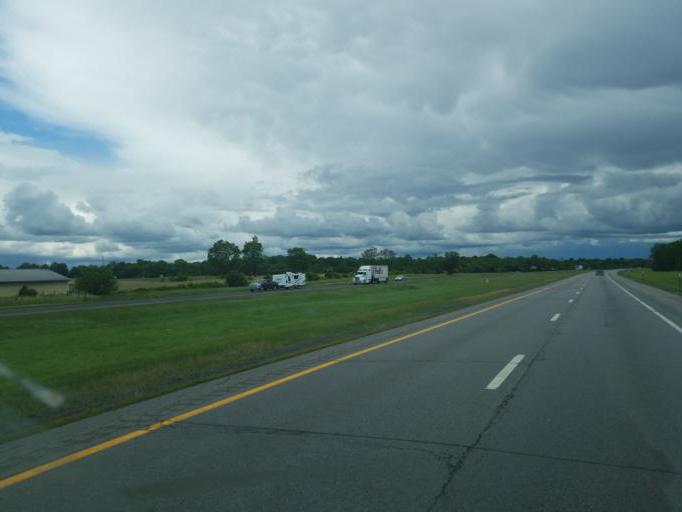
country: US
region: New York
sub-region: Ontario County
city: Phelps
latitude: 42.9742
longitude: -77.0975
